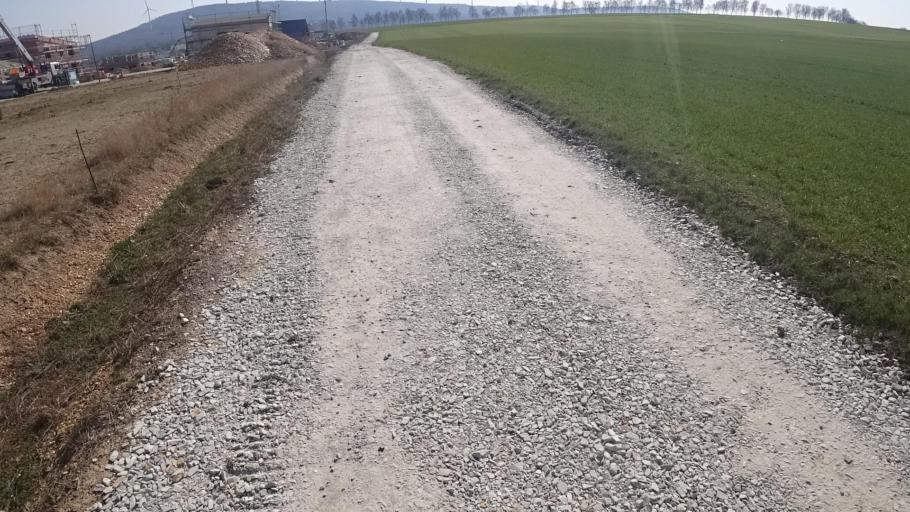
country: DE
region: Rheinland-Pfalz
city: Rheinbollen
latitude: 50.0082
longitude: 7.6582
